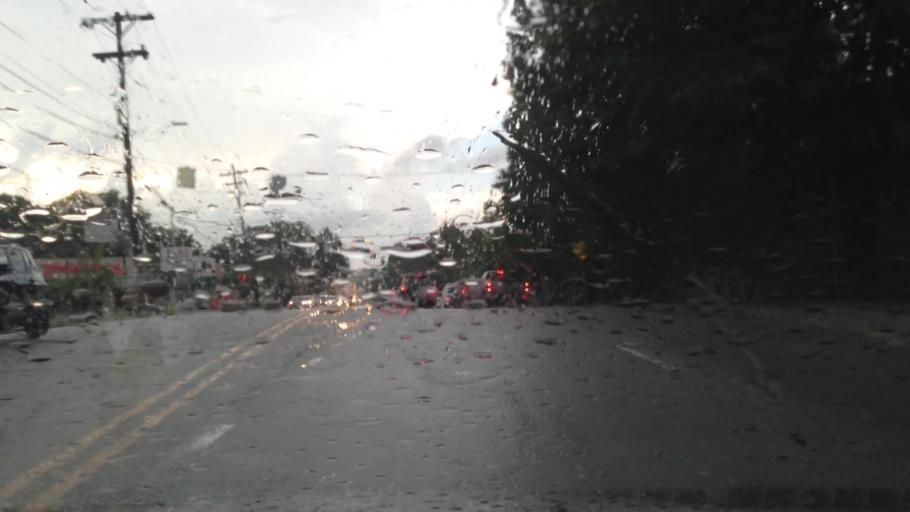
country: US
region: North Carolina
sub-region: Guilford County
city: Greensboro
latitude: 36.0636
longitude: -79.8154
